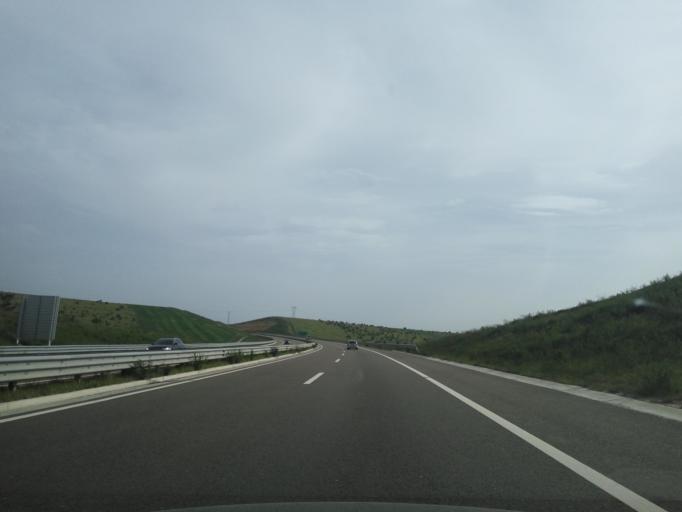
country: XK
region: Prizren
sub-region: Komuna e Malisheves
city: Llazice
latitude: 42.5356
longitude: 20.8022
